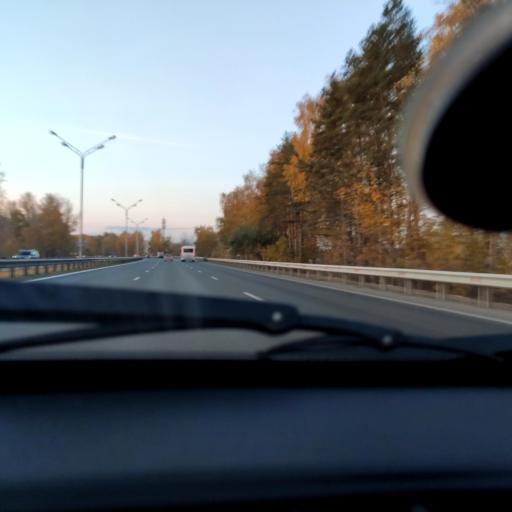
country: RU
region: Bashkortostan
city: Ufa
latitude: 54.6281
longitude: 55.9261
